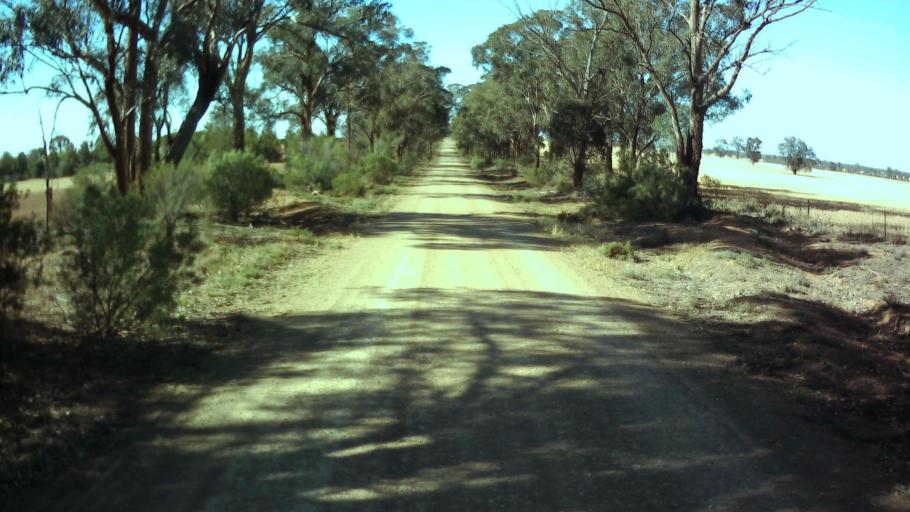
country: AU
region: New South Wales
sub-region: Weddin
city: Grenfell
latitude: -33.9030
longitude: 147.8782
